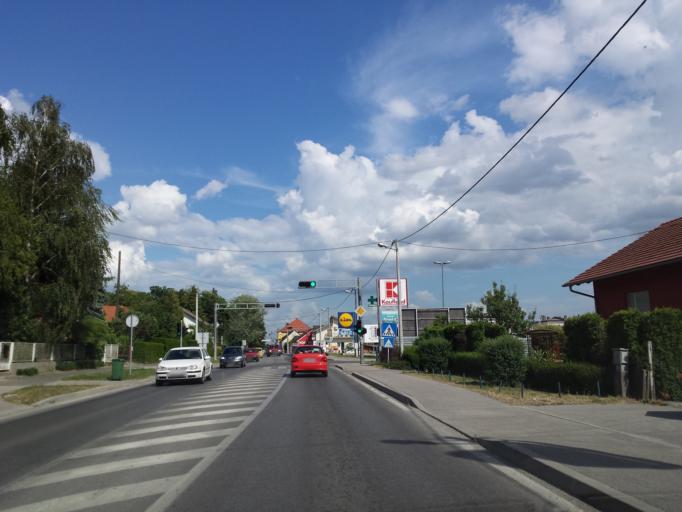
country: HR
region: Zagrebacka
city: Brckovljani
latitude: 45.8069
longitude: 16.2256
